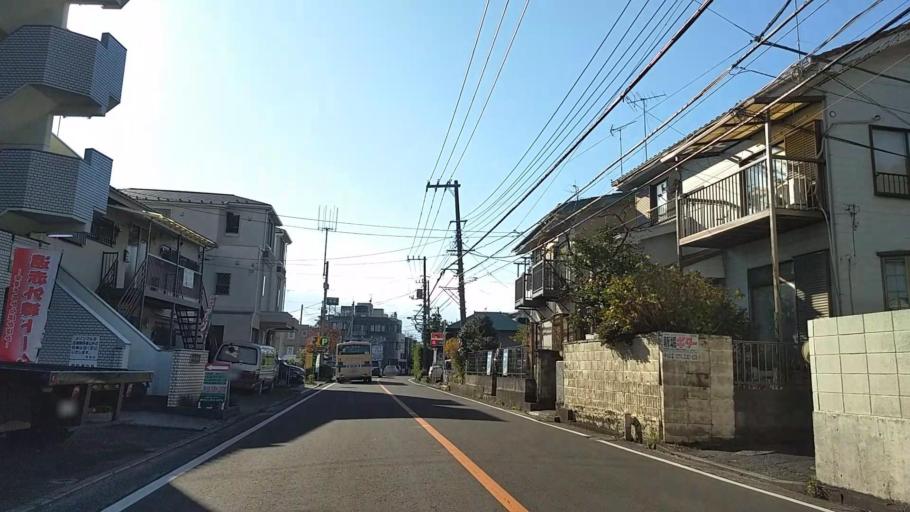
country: JP
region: Kanagawa
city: Yokohama
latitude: 35.5201
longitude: 139.5660
